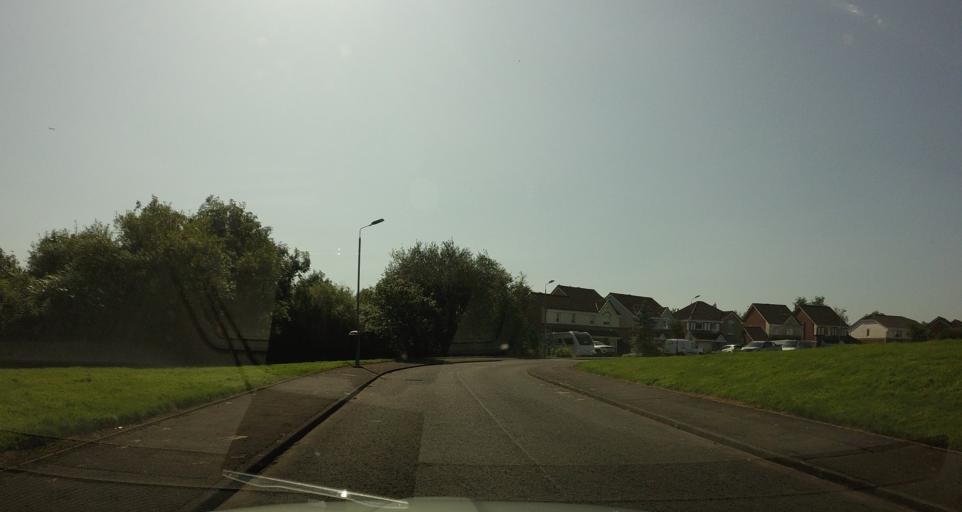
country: GB
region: Scotland
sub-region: South Lanarkshire
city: East Kilbride
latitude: 55.7405
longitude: -4.1944
